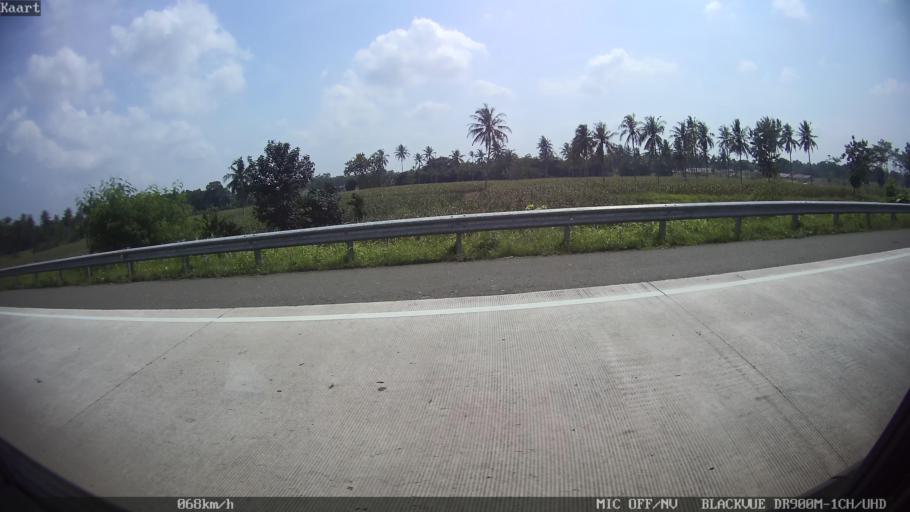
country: ID
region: Lampung
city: Natar
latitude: -5.3058
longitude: 105.2471
